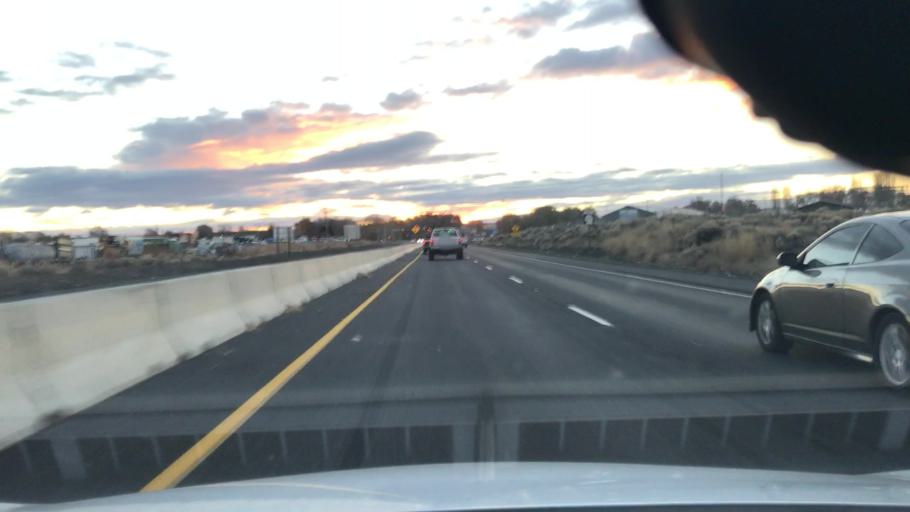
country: US
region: Washington
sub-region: Grant County
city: Moses Lake
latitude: 47.1411
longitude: -119.2674
